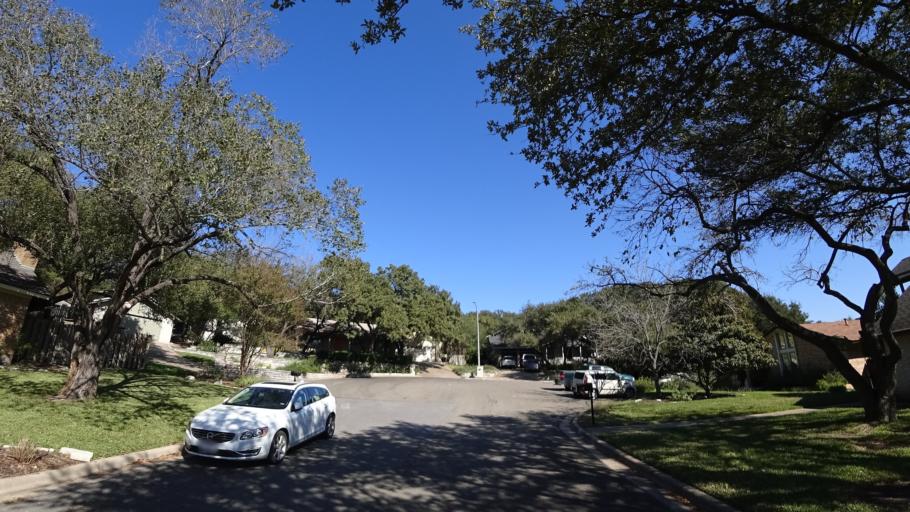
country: US
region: Texas
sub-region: Williamson County
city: Jollyville
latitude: 30.4216
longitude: -97.7650
